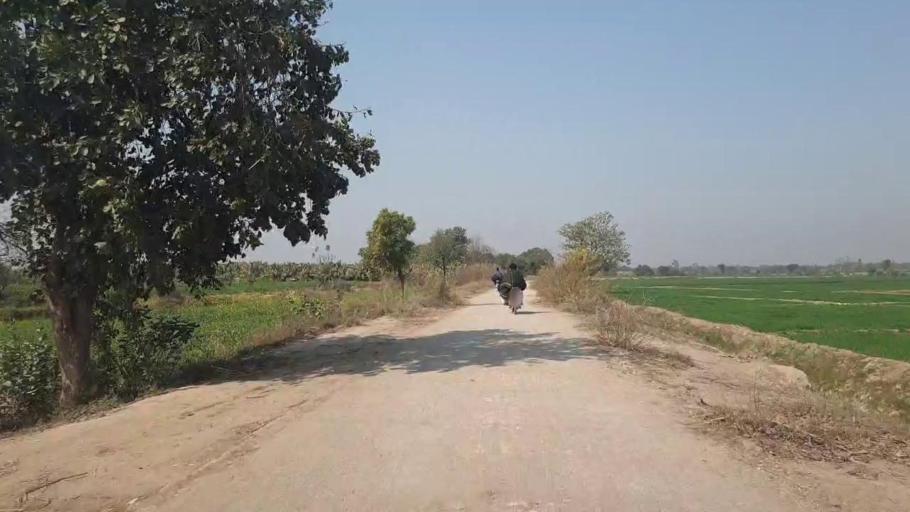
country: PK
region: Sindh
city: Tando Jam
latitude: 25.3284
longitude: 68.6047
